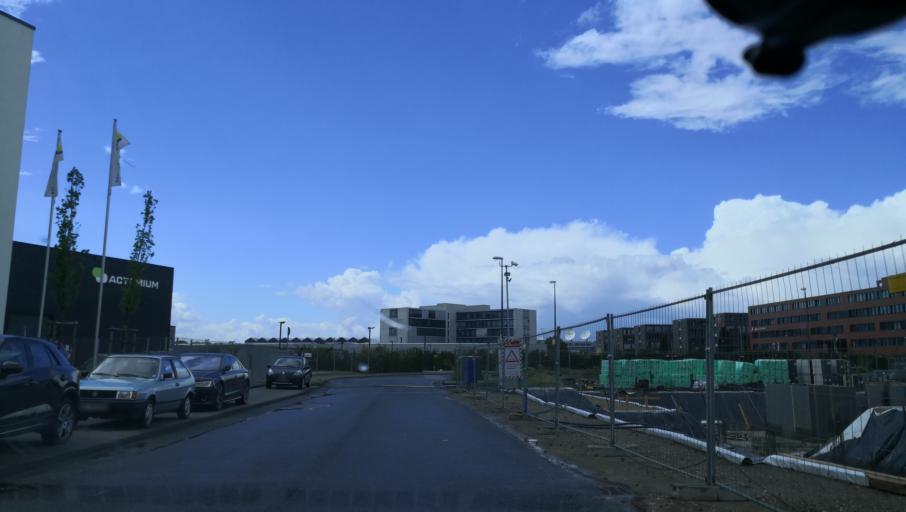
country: DE
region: North Rhine-Westphalia
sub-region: Regierungsbezirk Koln
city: Mengenich
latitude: 50.9822
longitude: 6.8919
